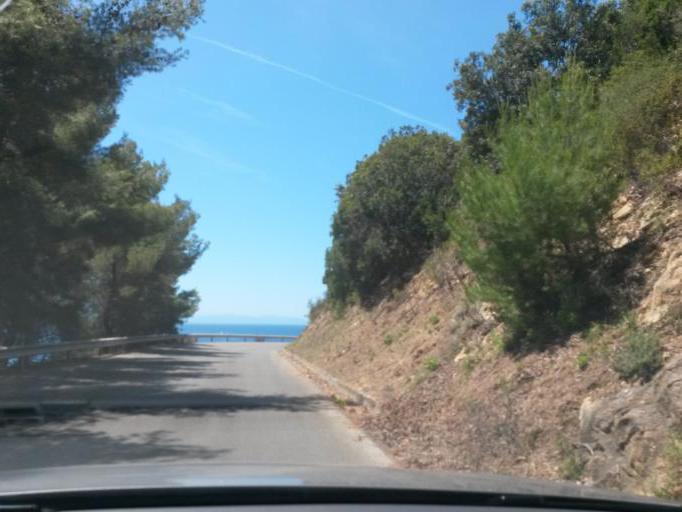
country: IT
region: Tuscany
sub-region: Provincia di Livorno
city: Portoferraio
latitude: 42.8214
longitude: 10.2747
